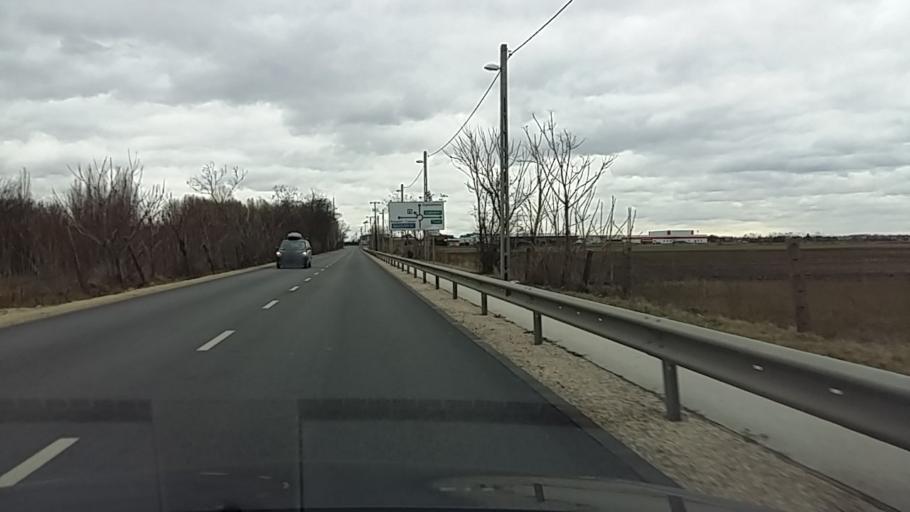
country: HU
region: Pest
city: Szigetszentmiklos
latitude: 47.3670
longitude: 19.0180
